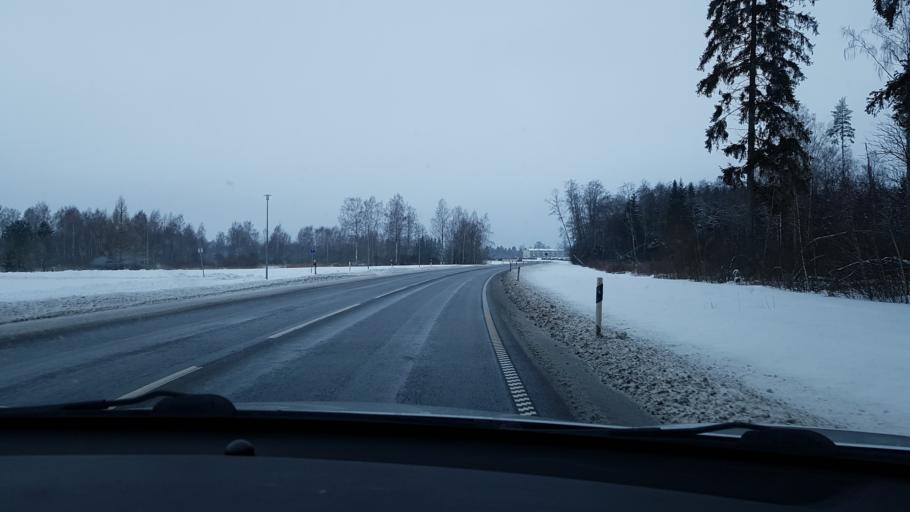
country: EE
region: Jaervamaa
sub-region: Tueri vald
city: Tueri
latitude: 58.8320
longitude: 25.4679
